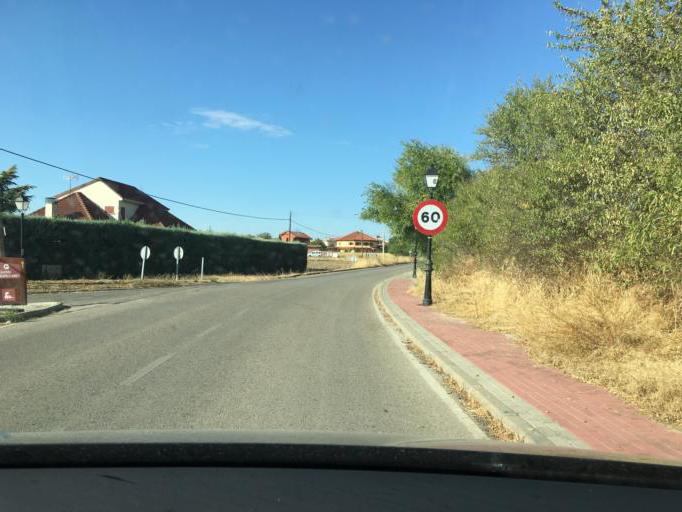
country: ES
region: Madrid
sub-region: Provincia de Madrid
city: Torremocha de Jarama
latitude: 40.8375
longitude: -3.4913
